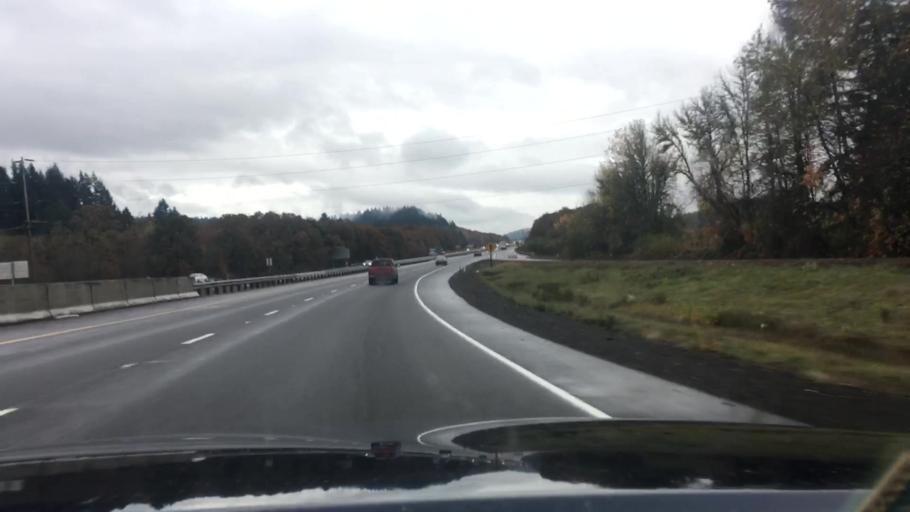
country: US
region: Oregon
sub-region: Lane County
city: Springfield
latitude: 43.9949
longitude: -123.0051
